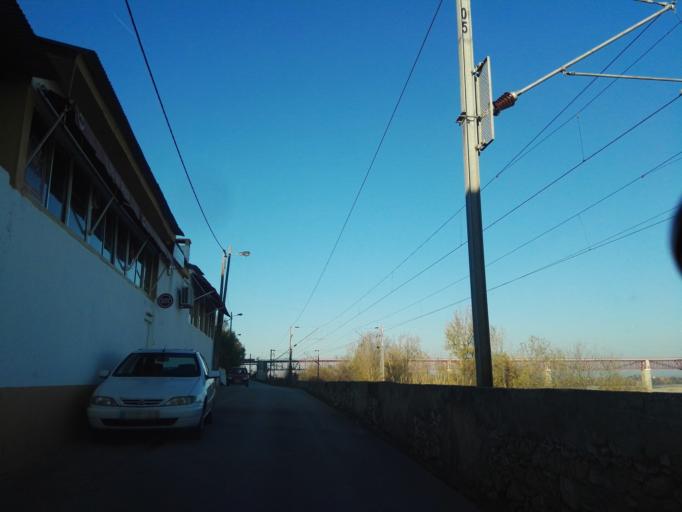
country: PT
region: Santarem
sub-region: Santarem
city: Santarem
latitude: 39.2309
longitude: -8.6744
